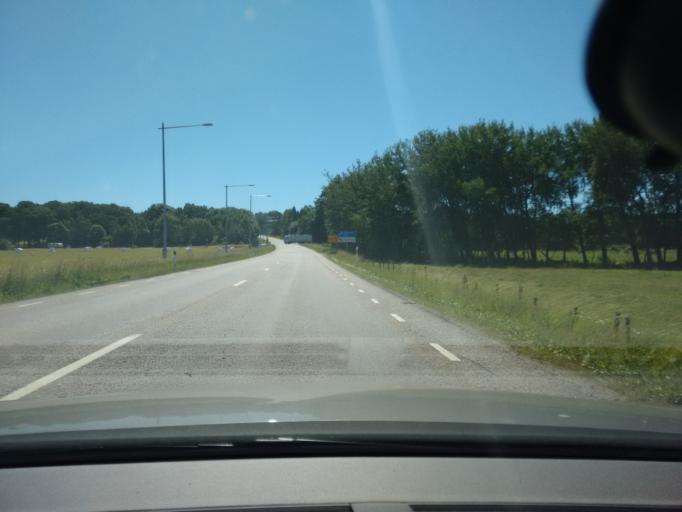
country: SE
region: Skane
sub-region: Horby Kommun
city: Hoerby
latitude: 55.8471
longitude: 13.6465
